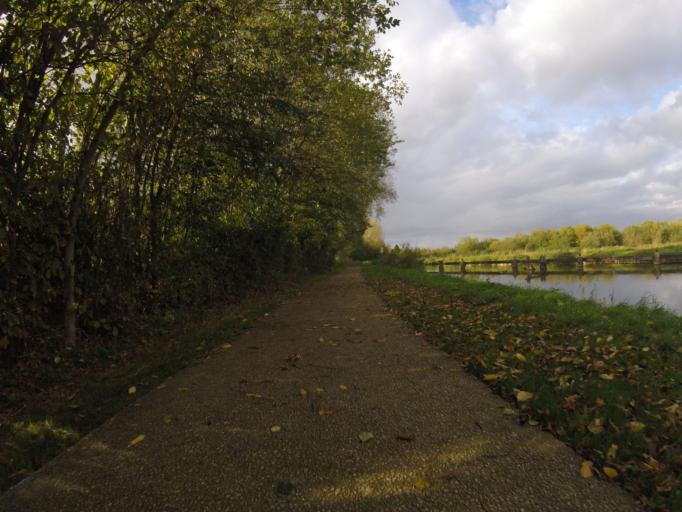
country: FR
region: Nord-Pas-de-Calais
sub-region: Departement du Pas-de-Calais
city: Sailly-sur-la-Lys
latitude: 50.6624
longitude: 2.7931
